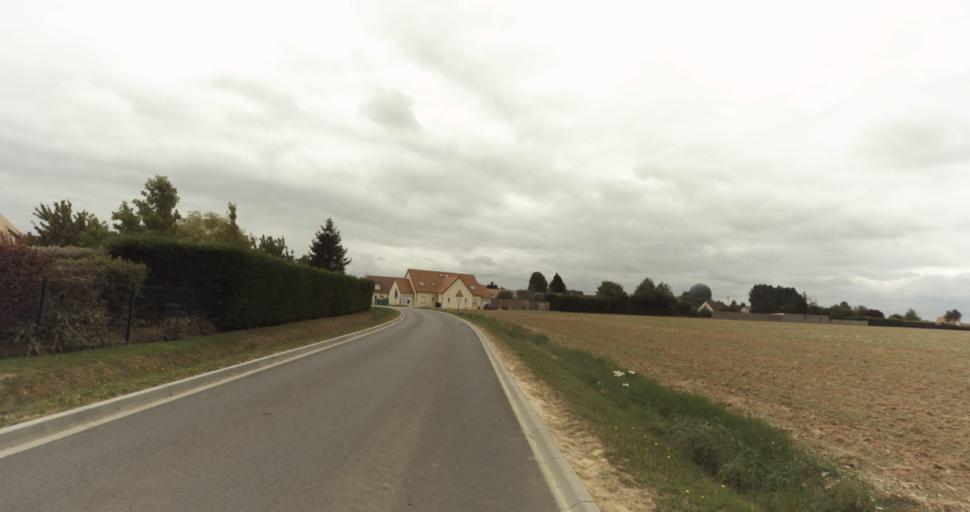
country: FR
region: Haute-Normandie
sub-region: Departement de l'Eure
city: Gravigny
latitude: 49.0342
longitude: 1.2399
